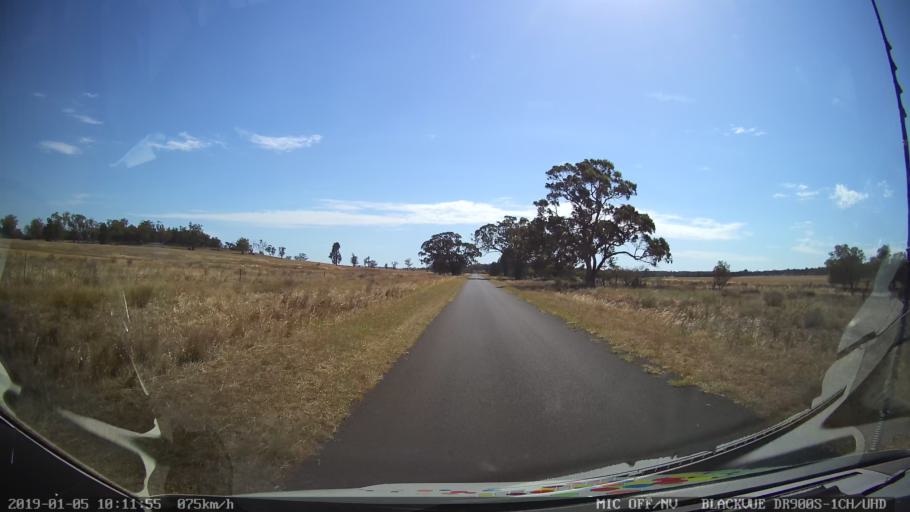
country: AU
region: New South Wales
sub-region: Gilgandra
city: Gilgandra
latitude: -31.6106
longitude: 148.9069
